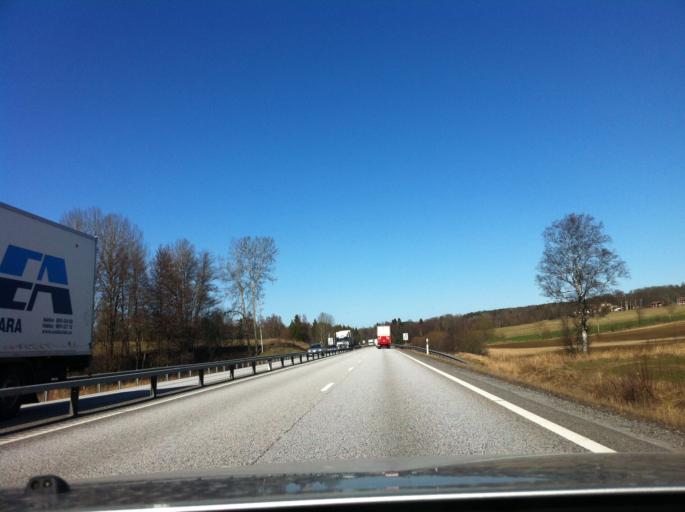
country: SE
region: Joenkoeping
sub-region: Jonkopings Kommun
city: Bankeryd
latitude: 57.8120
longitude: 14.0996
